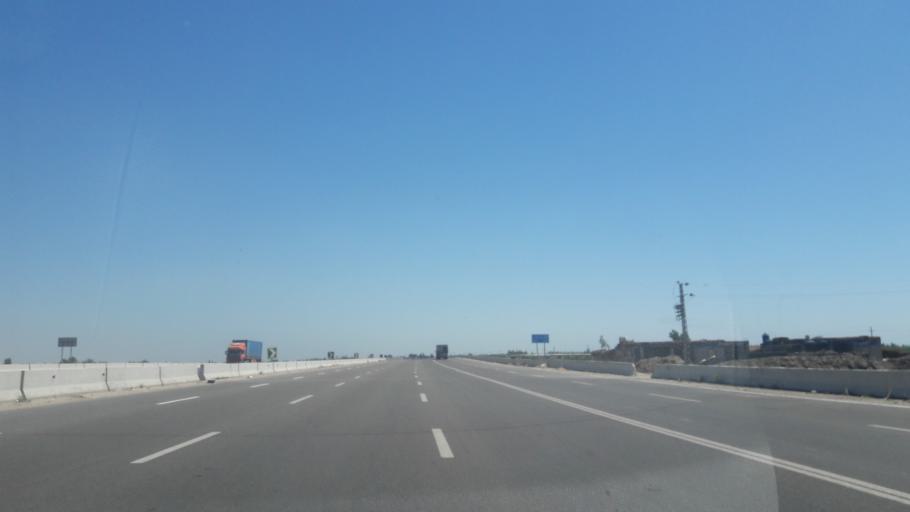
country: EG
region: Muhafazat Bur Sa`id
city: Port Said
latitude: 31.1575
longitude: 32.2353
